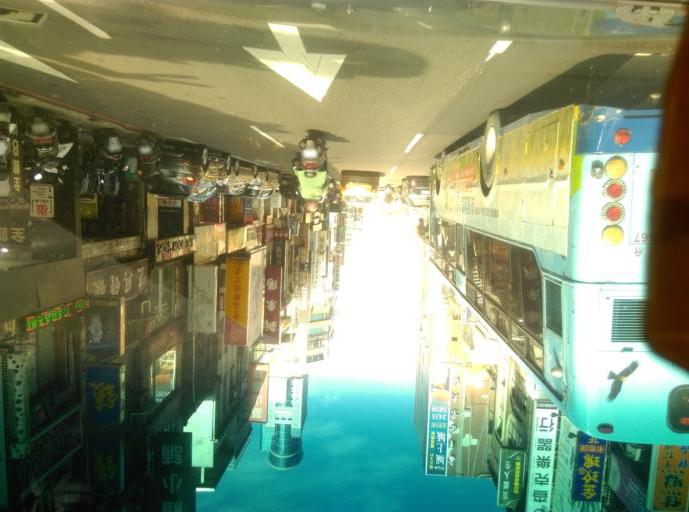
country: TW
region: Taiwan
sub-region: Keelung
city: Keelung
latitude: 25.1287
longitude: 121.7428
